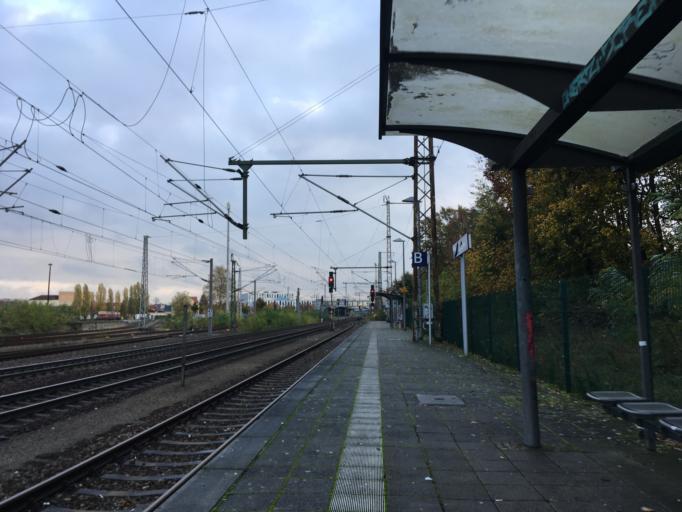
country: DE
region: Brandenburg
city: Furstenwalde
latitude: 52.3679
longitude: 14.0550
